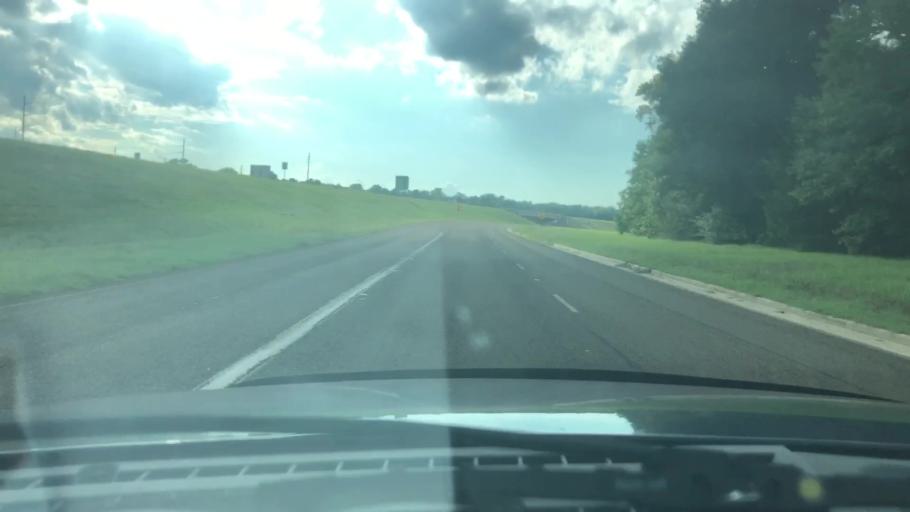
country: US
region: Texas
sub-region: Bowie County
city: Wake Village
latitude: 33.3865
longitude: -94.0878
